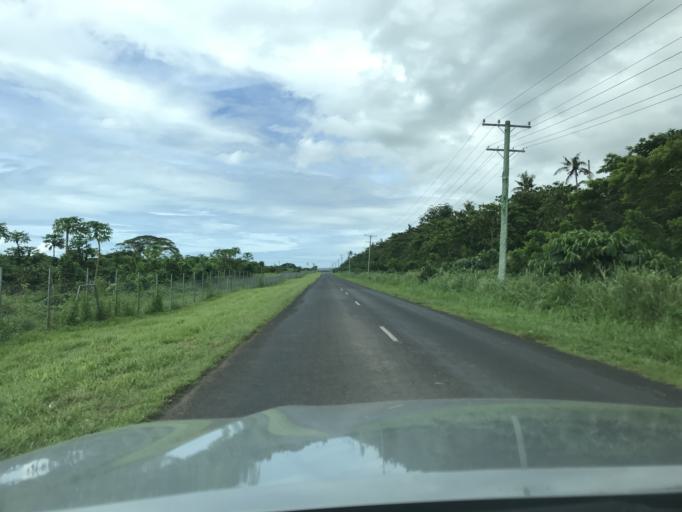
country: WS
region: Aiga-i-le-Tai
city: Mulifanua
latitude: -13.8339
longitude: -172.0099
